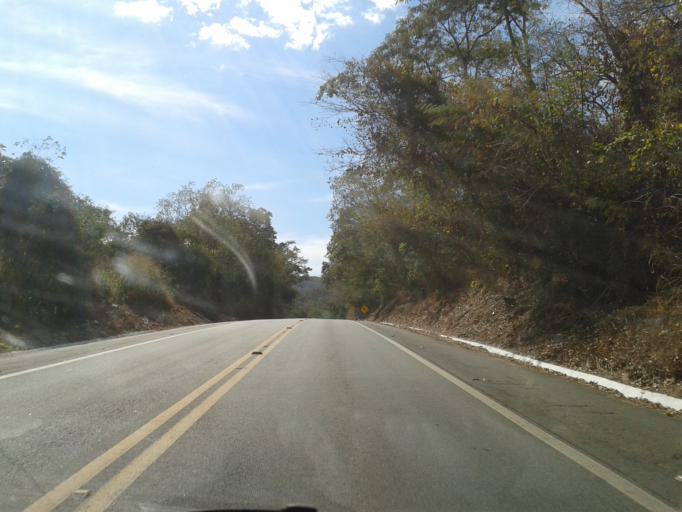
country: BR
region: Goias
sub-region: Goias
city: Goias
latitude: -15.9370
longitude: -50.1345
